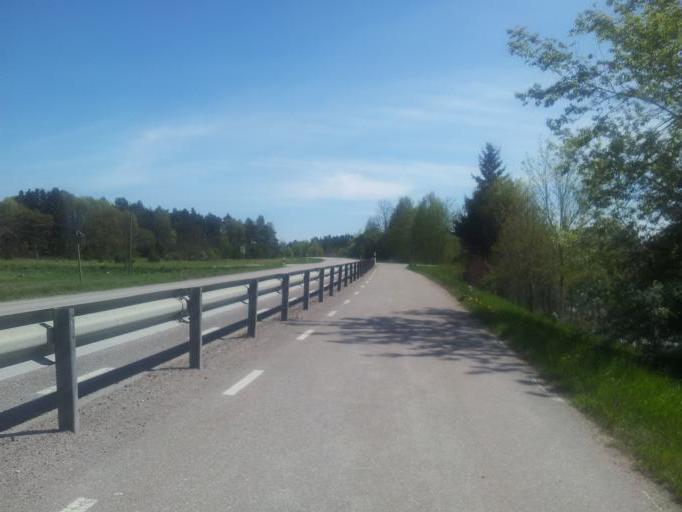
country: SE
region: Uppsala
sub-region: Uppsala Kommun
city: Alsike
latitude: 59.8552
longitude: 17.8265
